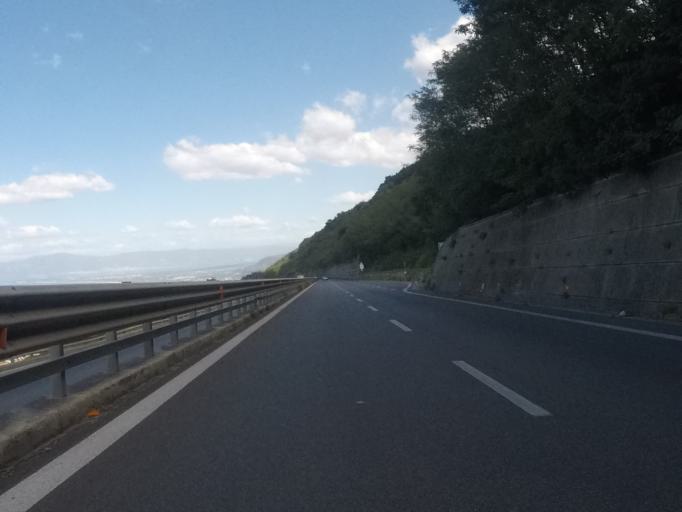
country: IT
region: Calabria
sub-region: Provincia di Vibo-Valentia
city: Maierato
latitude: 38.7201
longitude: 16.1568
